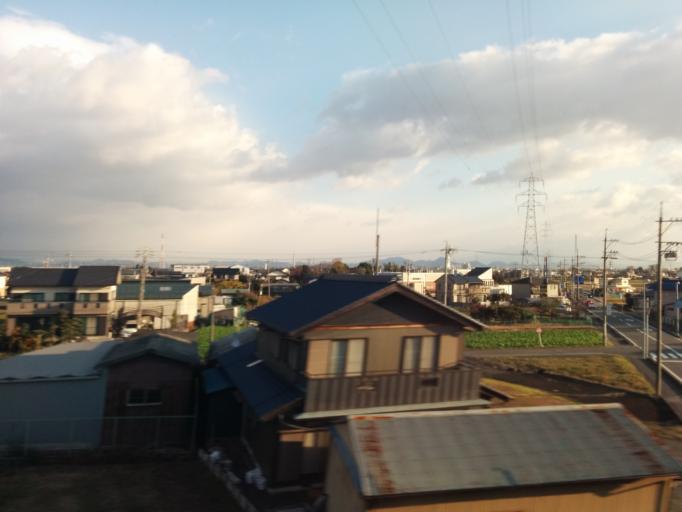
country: JP
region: Gifu
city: Ogaki
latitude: 35.3387
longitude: 136.6548
